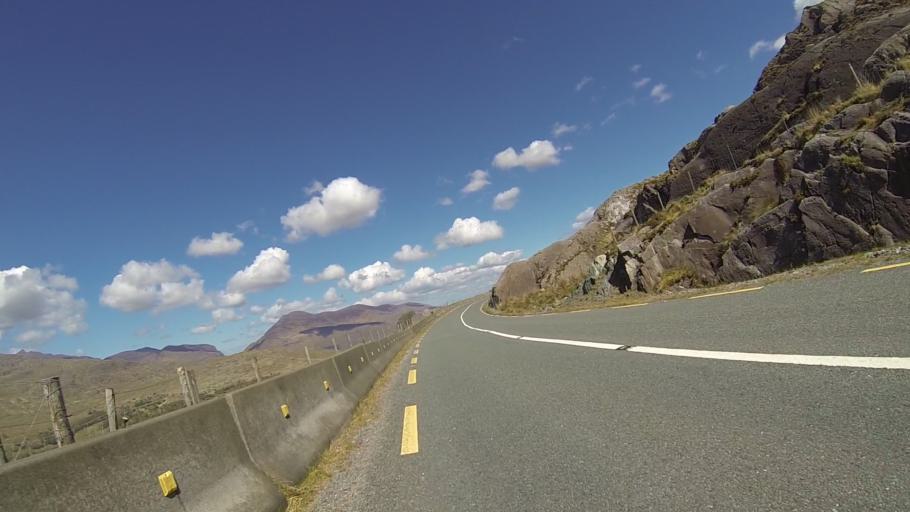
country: IE
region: Munster
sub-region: Ciarrai
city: Kenmare
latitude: 51.9411
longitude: -9.6537
